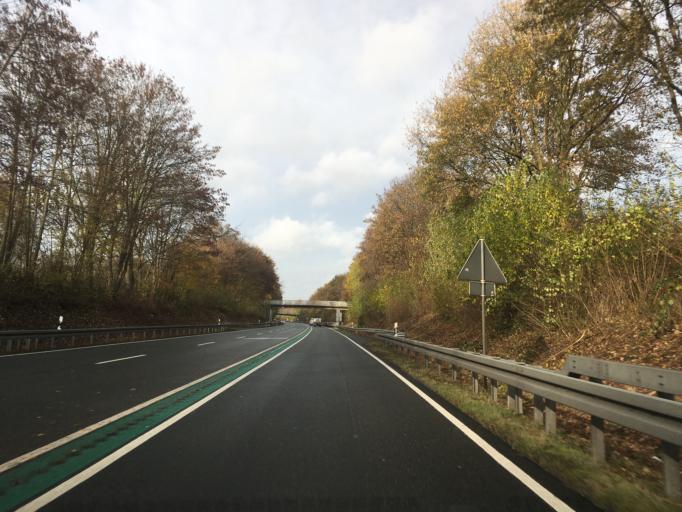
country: DE
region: North Rhine-Westphalia
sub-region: Regierungsbezirk Munster
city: Steinfurt
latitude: 52.1525
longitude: 7.3554
